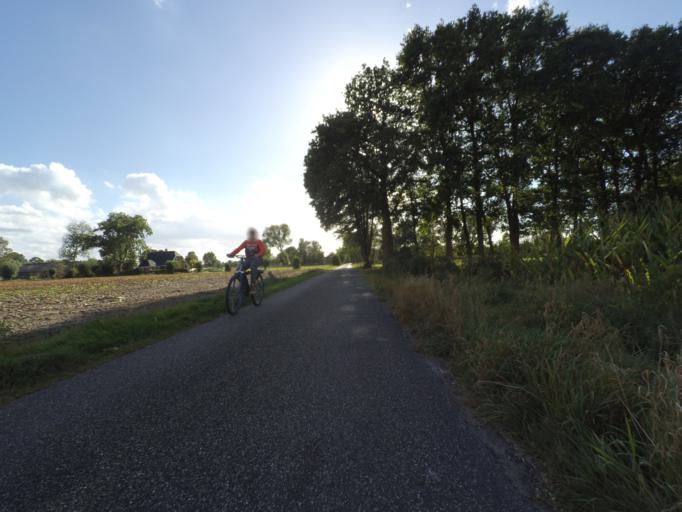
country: NL
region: Gelderland
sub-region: Gemeente Ede
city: Ederveen
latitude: 52.0734
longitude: 5.5708
